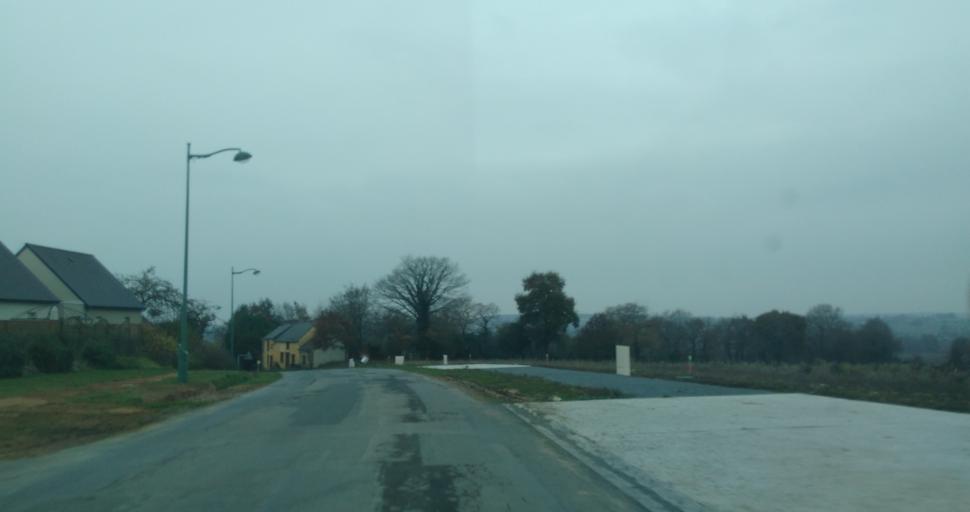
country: FR
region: Brittany
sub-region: Departement d'Ille-et-Vilaine
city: Iffendic
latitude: 48.0936
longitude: -2.1012
